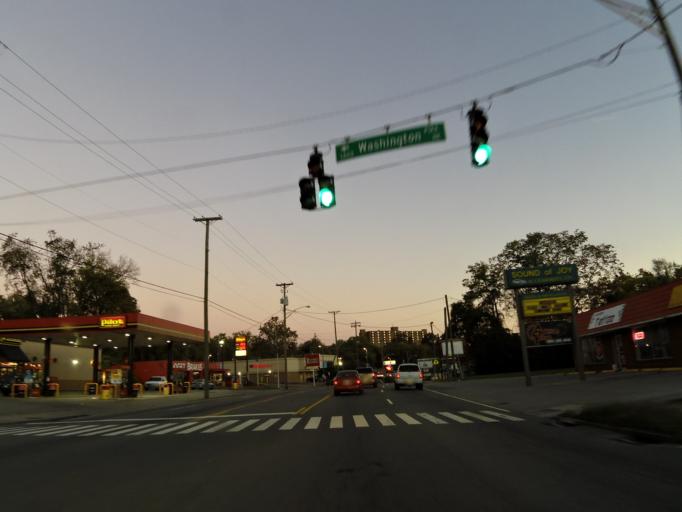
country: US
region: Tennessee
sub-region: Knox County
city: Knoxville
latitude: 35.9958
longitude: -83.9225
